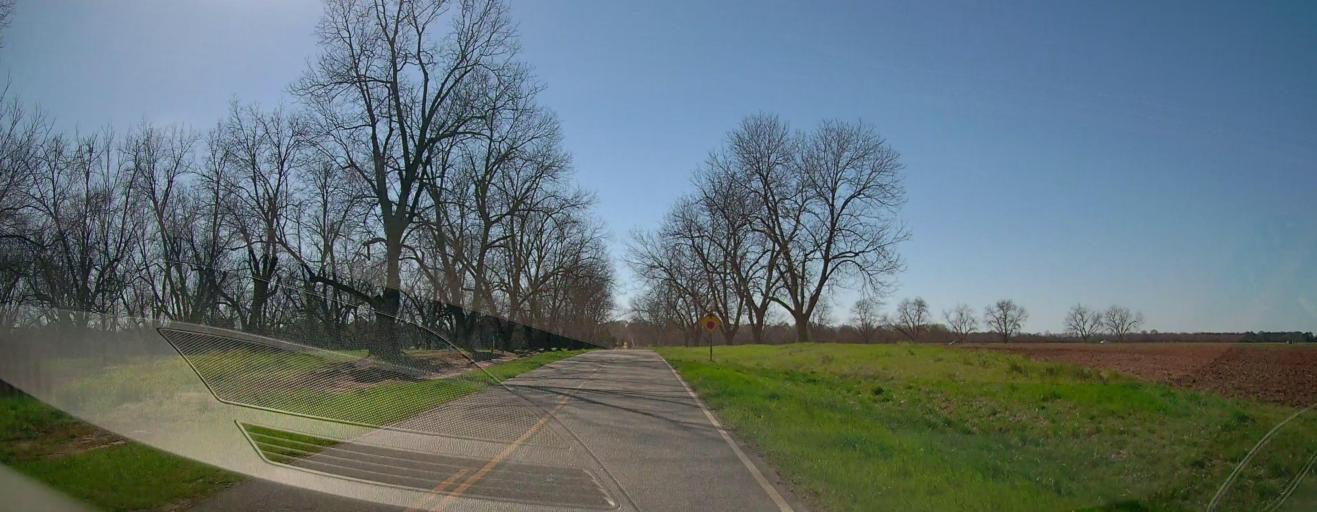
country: US
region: Georgia
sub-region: Peach County
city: Fort Valley
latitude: 32.6442
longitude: -83.8608
